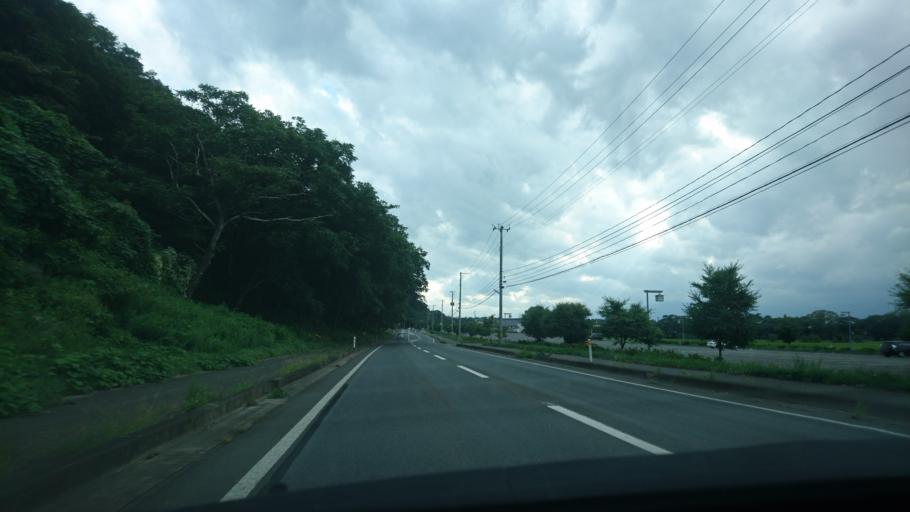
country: JP
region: Iwate
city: Kitakami
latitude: 39.2748
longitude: 141.1305
